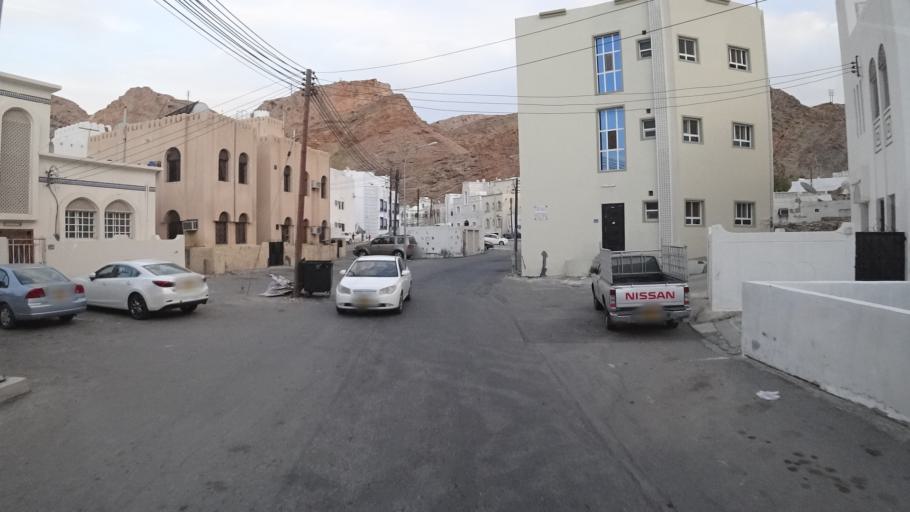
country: OM
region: Muhafazat Masqat
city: Muscat
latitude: 23.5761
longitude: 58.5473
